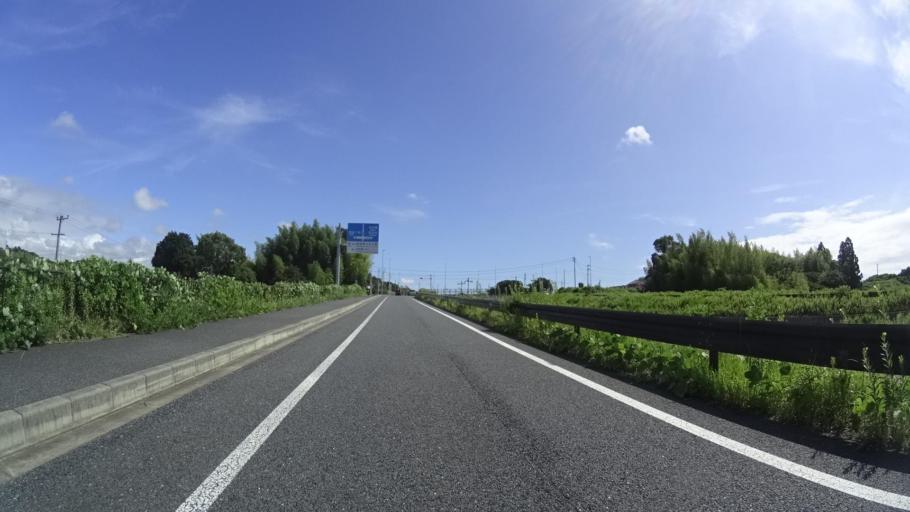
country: JP
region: Mie
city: Kawage
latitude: 34.8421
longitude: 136.5476
